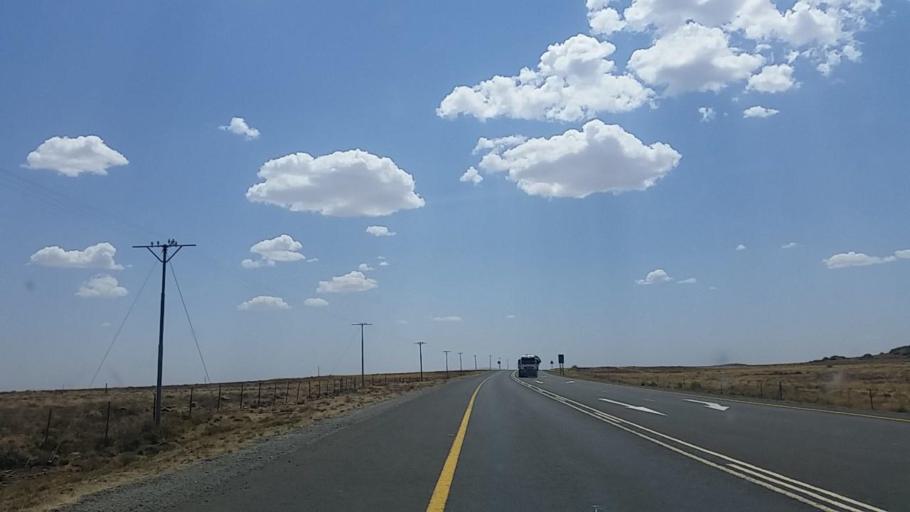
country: ZA
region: Northern Cape
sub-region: Pixley ka Seme District Municipality
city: Noupoort
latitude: -31.1009
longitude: 24.9540
